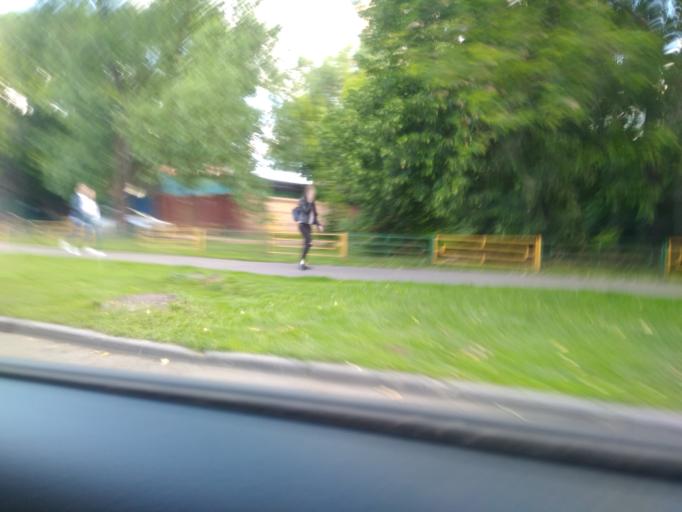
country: RU
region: Moskovskaya
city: Koptevo
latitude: 55.8343
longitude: 37.5326
